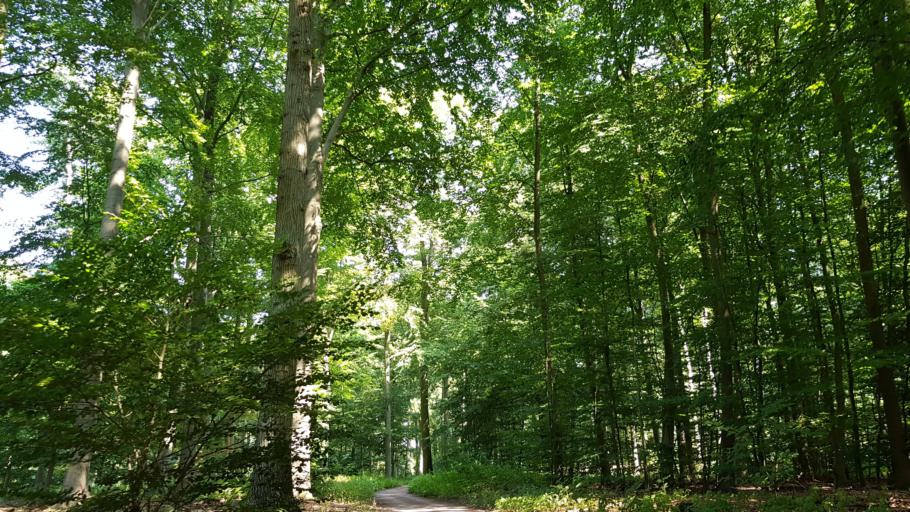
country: DE
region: Lower Saxony
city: Adendorf
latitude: 53.2697
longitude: 10.4346
